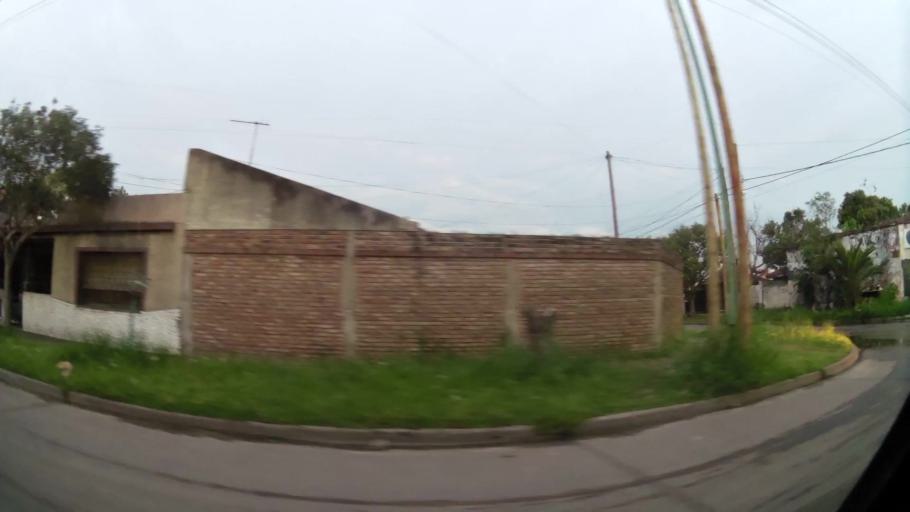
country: AR
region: Buenos Aires
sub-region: Partido de Lomas de Zamora
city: Lomas de Zamora
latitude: -34.7449
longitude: -58.3698
